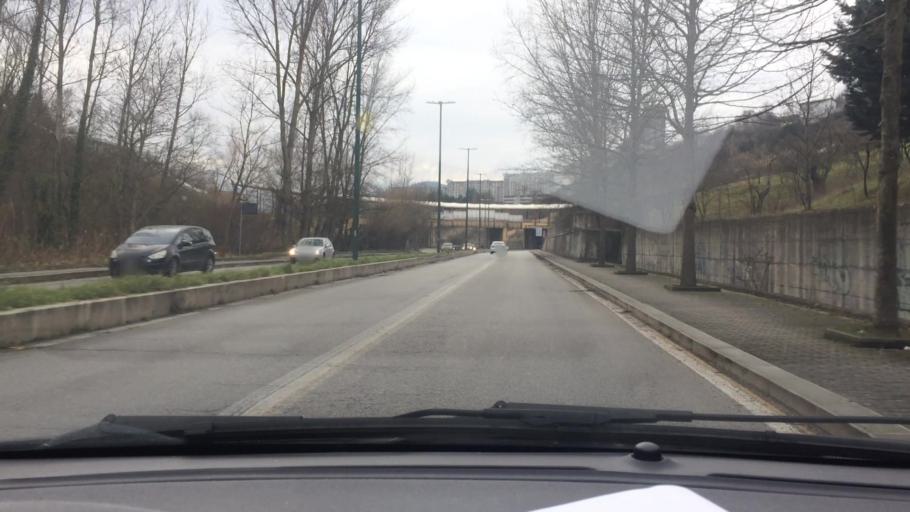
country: IT
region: Basilicate
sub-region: Provincia di Potenza
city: Potenza
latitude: 40.6387
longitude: 15.7964
